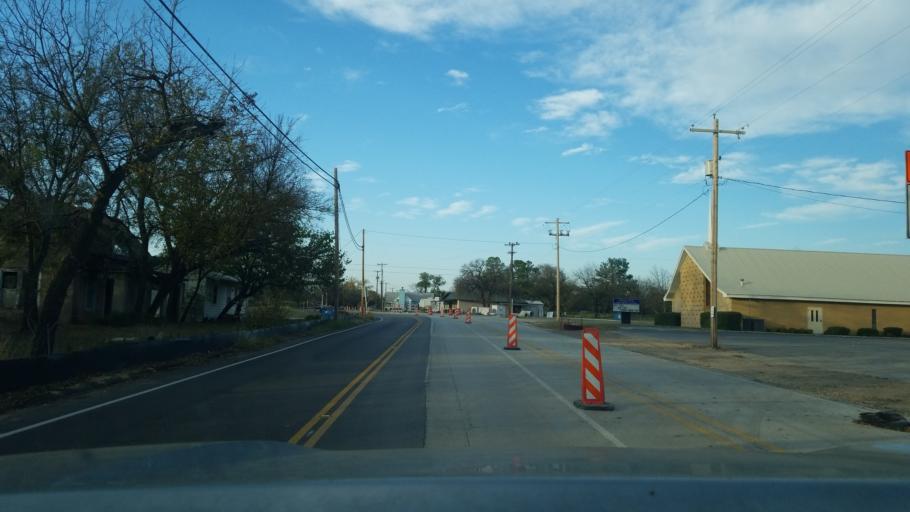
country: US
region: Texas
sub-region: Brown County
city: Lake Brownwood
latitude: 32.0984
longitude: -98.9640
